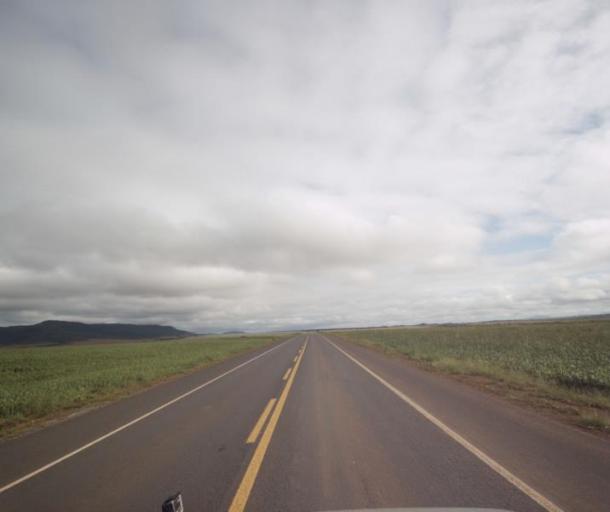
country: BR
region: Goias
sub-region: Padre Bernardo
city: Padre Bernardo
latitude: -15.4077
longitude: -48.6291
